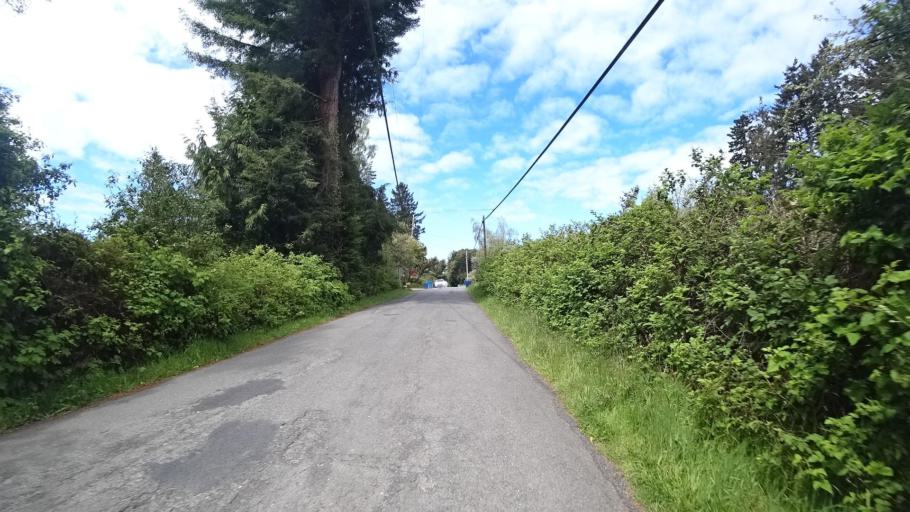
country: US
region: California
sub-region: Humboldt County
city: Bayside
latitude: 40.8491
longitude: -124.0595
